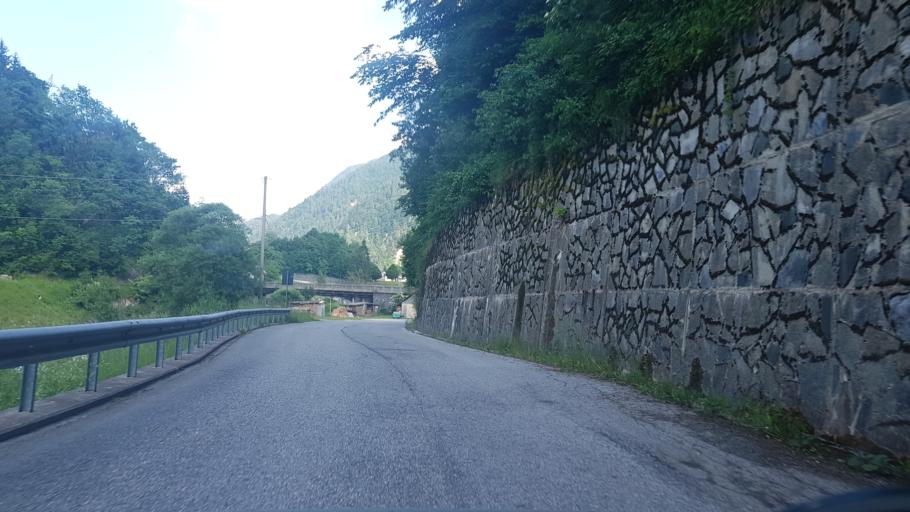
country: IT
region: Friuli Venezia Giulia
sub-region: Provincia di Udine
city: Pontebba
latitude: 46.5110
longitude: 13.2981
